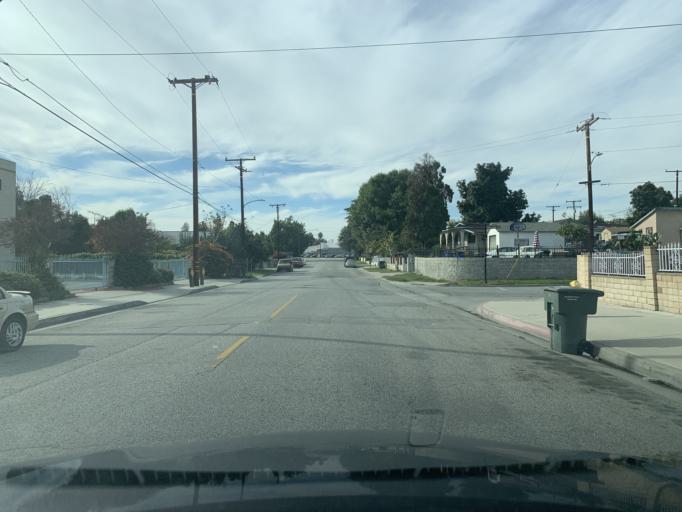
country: US
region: California
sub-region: Los Angeles County
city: El Monte
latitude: 34.0735
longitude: -118.0480
